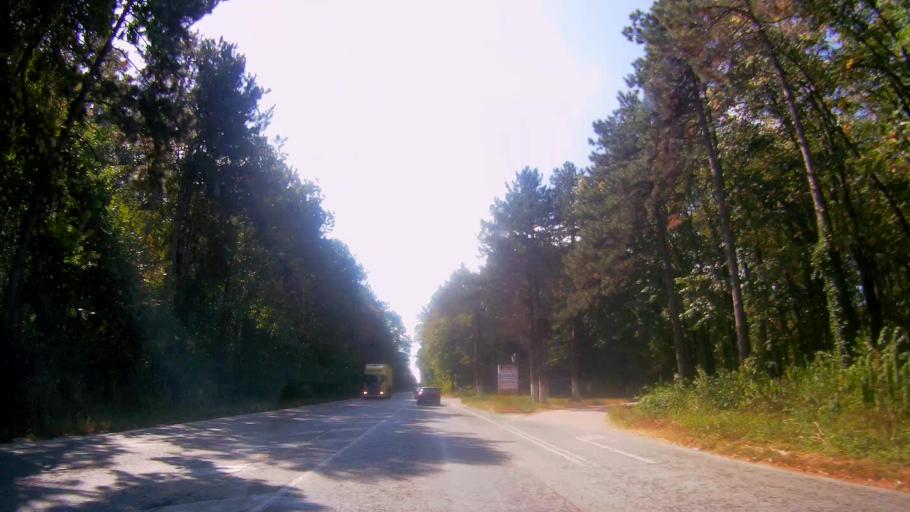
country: BG
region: Ruse
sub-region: Obshtina Borovo
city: Borovo
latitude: 43.5564
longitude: 25.8192
